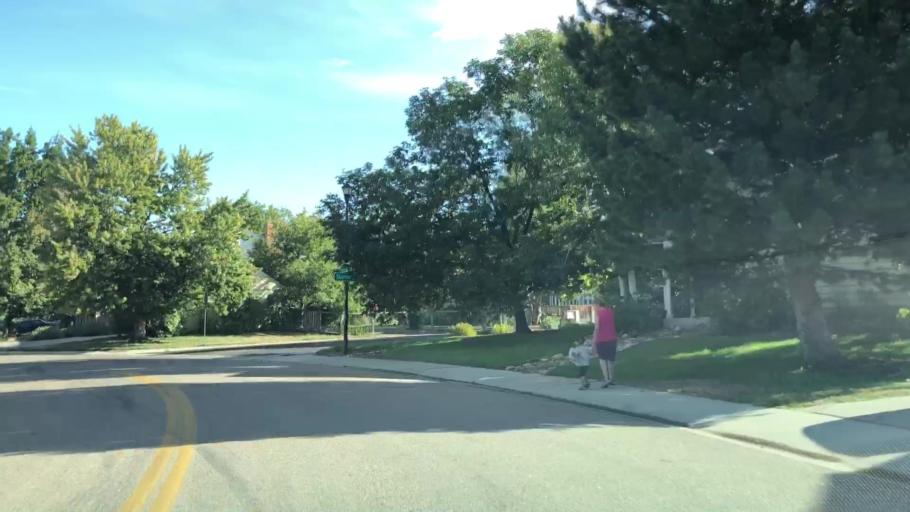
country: US
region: Colorado
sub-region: Larimer County
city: Fort Collins
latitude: 40.5289
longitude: -105.0453
